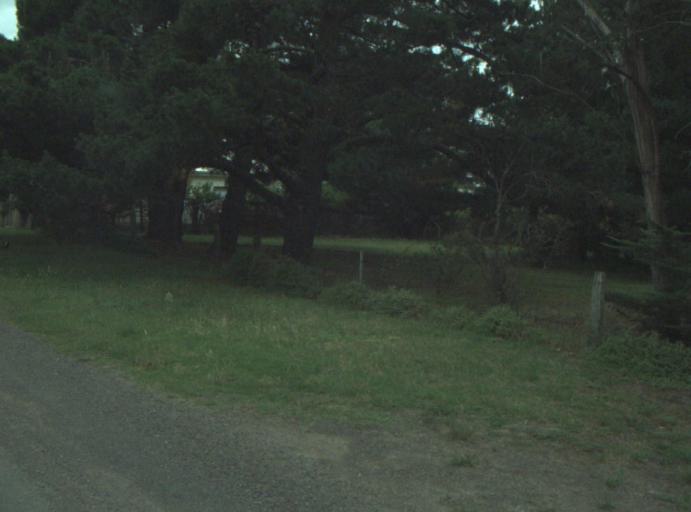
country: AU
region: Victoria
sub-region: Greater Geelong
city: Leopold
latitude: -38.2028
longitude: 144.4661
